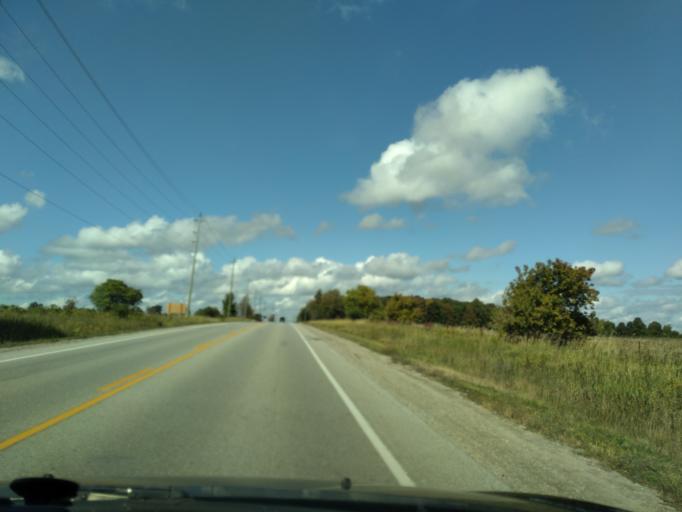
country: CA
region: Ontario
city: Innisfil
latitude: 44.2853
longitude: -79.5708
